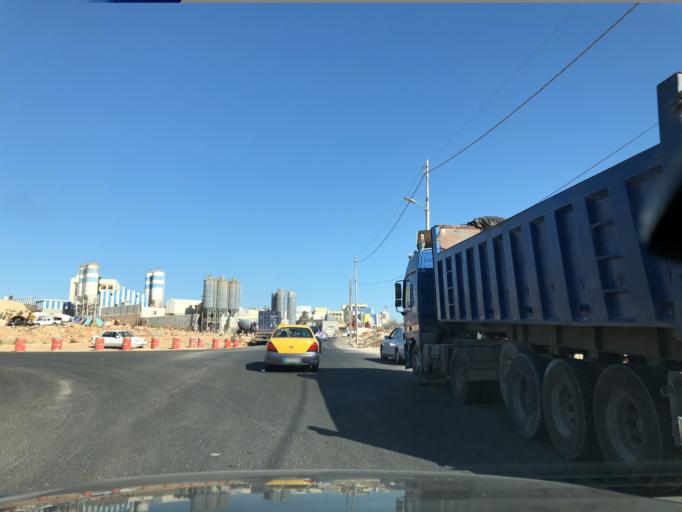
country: JO
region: Amman
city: Wadi as Sir
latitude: 31.9374
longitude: 35.8493
